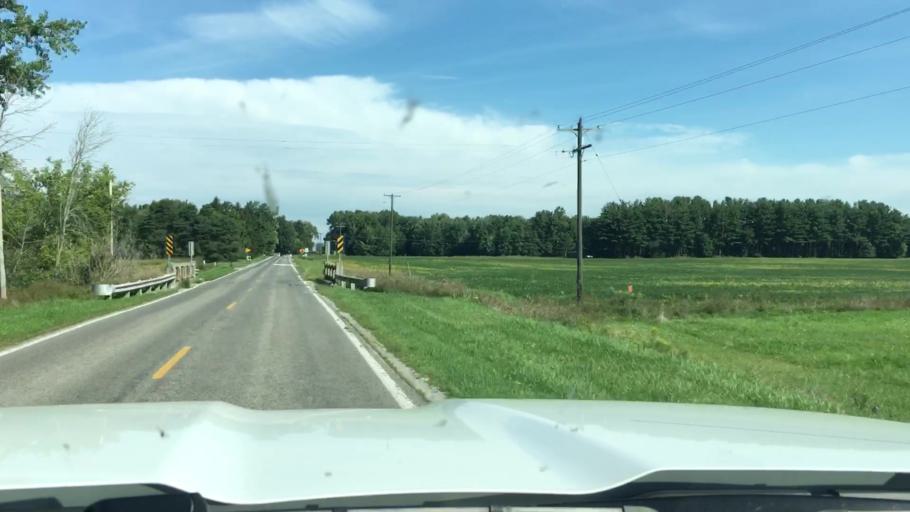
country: US
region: Michigan
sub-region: Saginaw County
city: Hemlock
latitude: 43.4779
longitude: -84.2303
